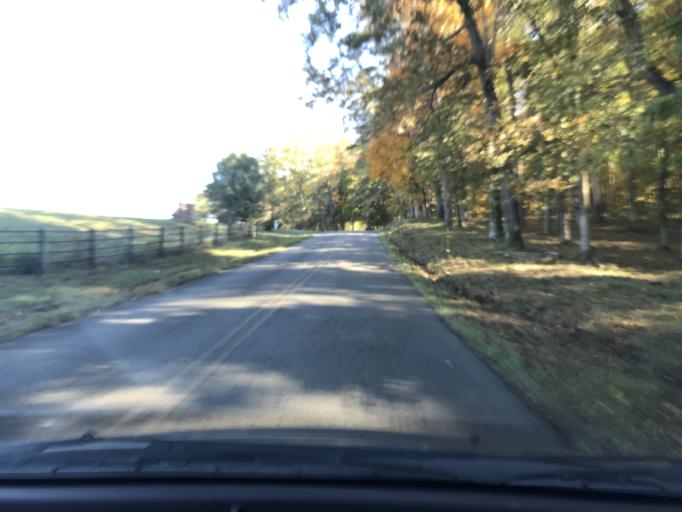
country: US
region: Georgia
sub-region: Dade County
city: Trenton
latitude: 34.8832
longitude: -85.4717
